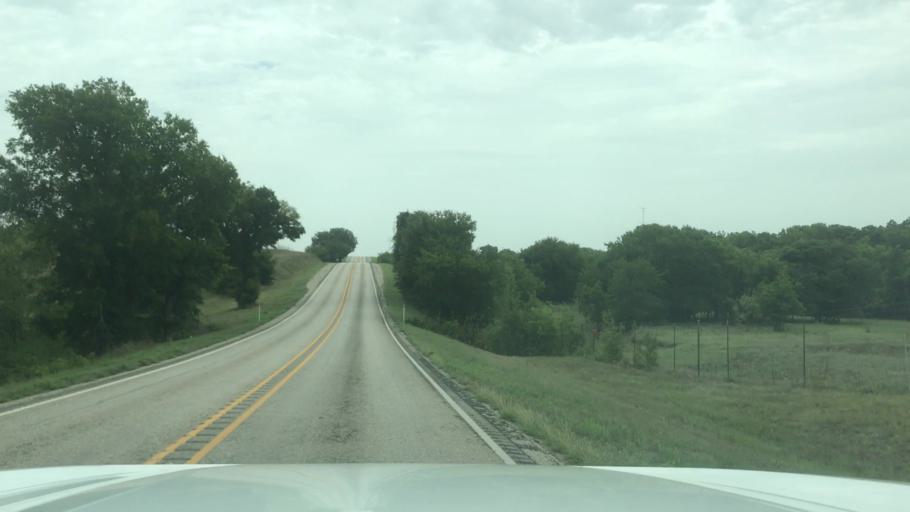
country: US
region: Texas
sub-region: Hamilton County
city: Hico
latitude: 32.0552
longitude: -98.1791
